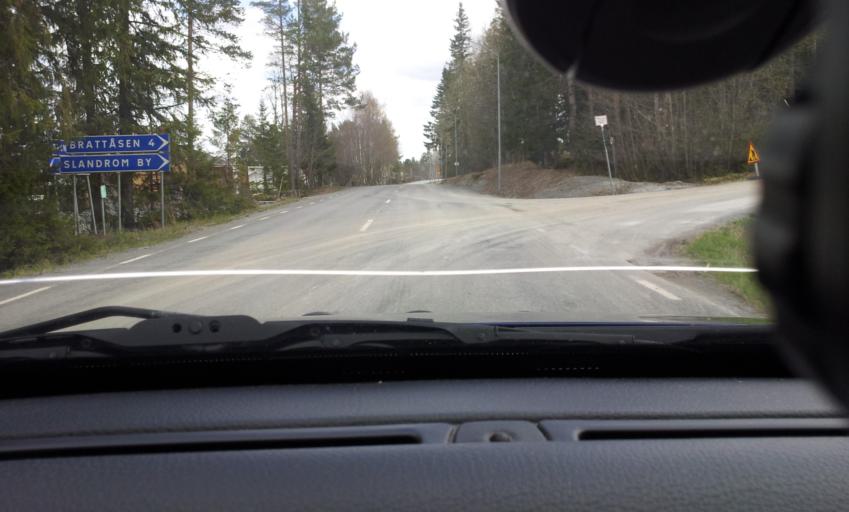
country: SE
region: Jaemtland
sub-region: OEstersunds Kommun
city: Ostersund
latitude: 63.1323
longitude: 14.6591
